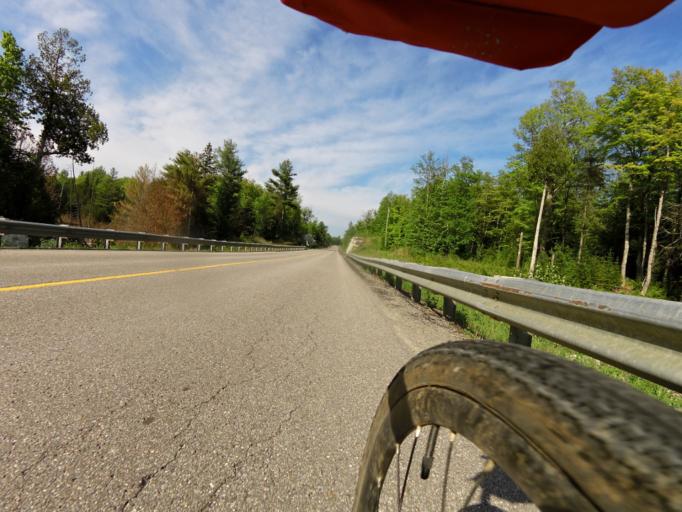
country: CA
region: Ontario
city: Arnprior
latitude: 45.1662
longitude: -76.4988
